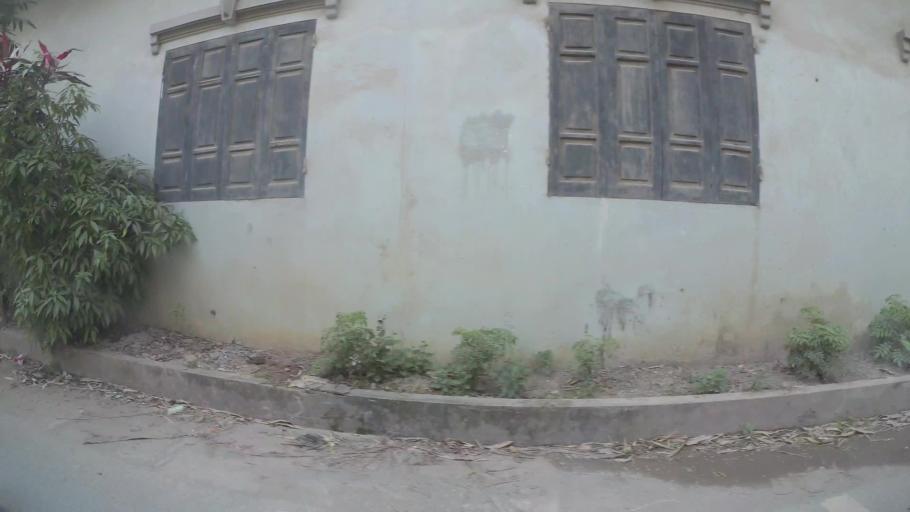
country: VN
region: Ha Noi
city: Ha Dong
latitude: 21.0025
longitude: 105.7584
